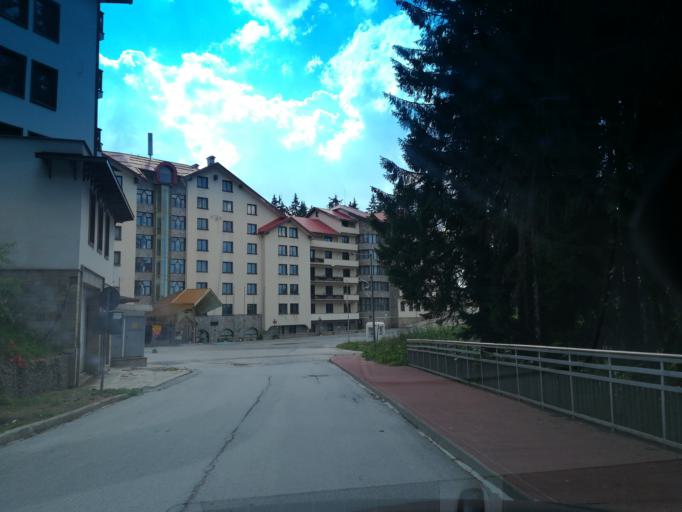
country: BG
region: Smolyan
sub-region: Obshtina Smolyan
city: Smolyan
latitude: 41.6556
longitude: 24.6920
